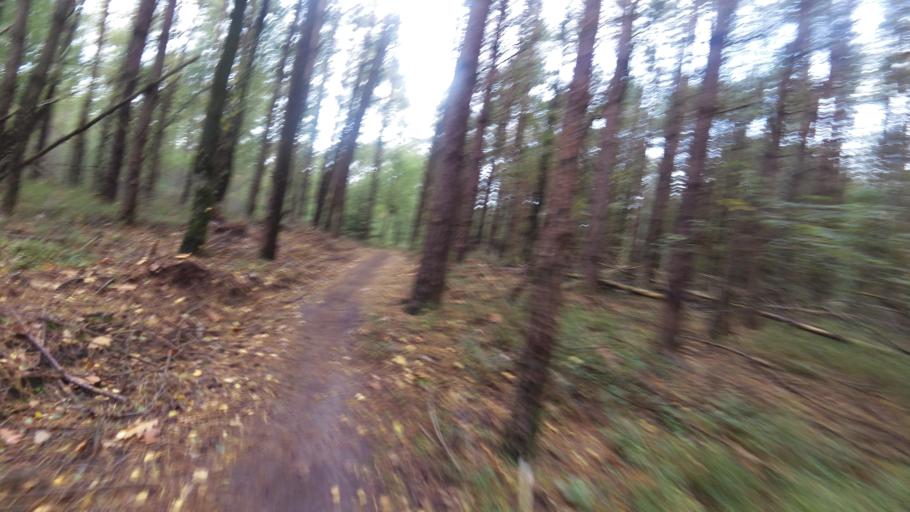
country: NL
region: Gelderland
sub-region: Gemeente Ede
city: Wekerom
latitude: 52.0727
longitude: 5.7130
